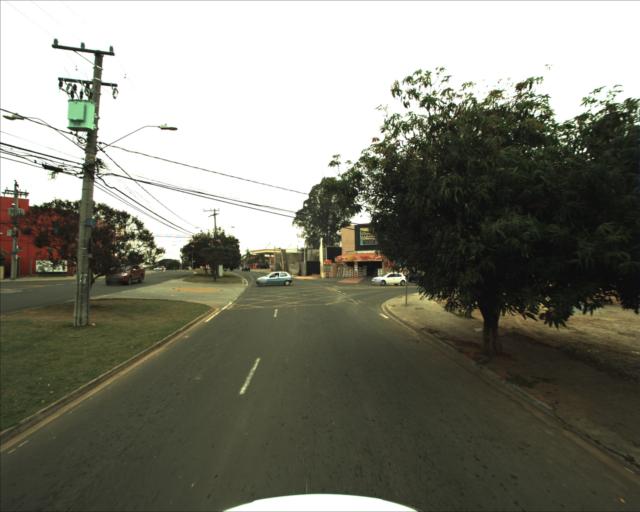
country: BR
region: Sao Paulo
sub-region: Sorocaba
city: Sorocaba
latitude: -23.4936
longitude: -47.5125
